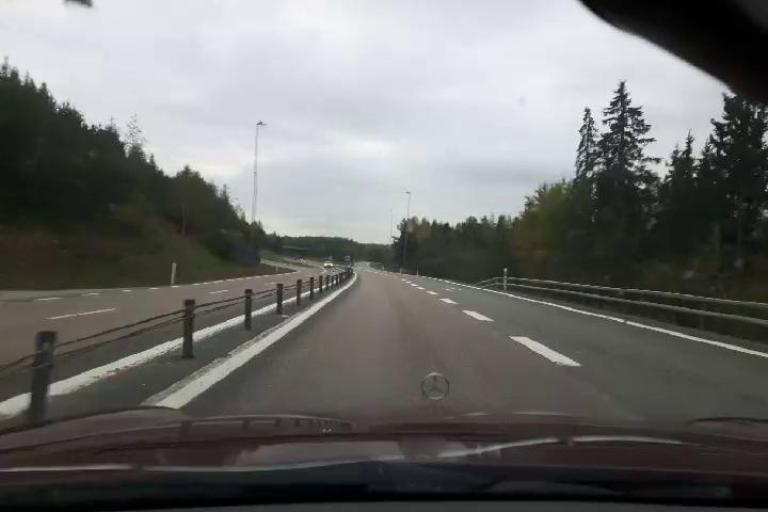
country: SE
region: Vaesternorrland
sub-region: Kramfors Kommun
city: Nordingra
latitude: 62.9333
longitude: 18.0950
